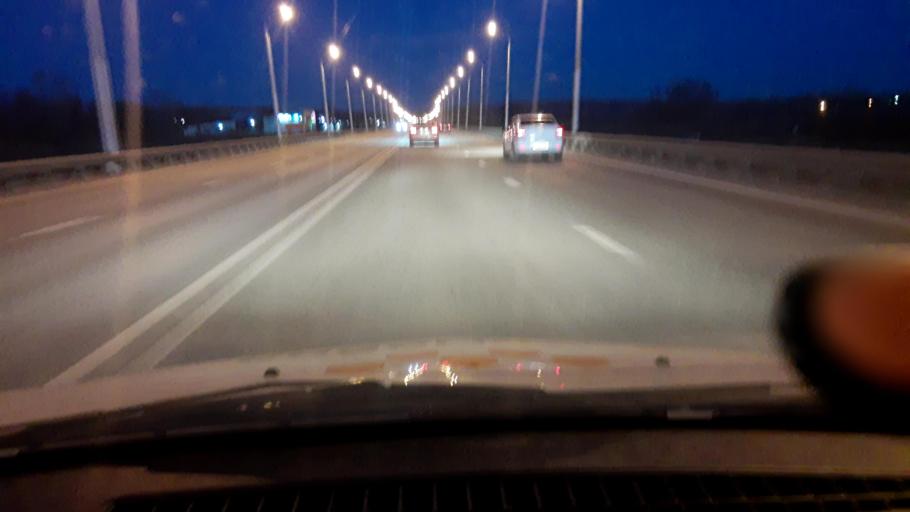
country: RU
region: Bashkortostan
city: Iglino
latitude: 54.8025
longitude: 56.1905
